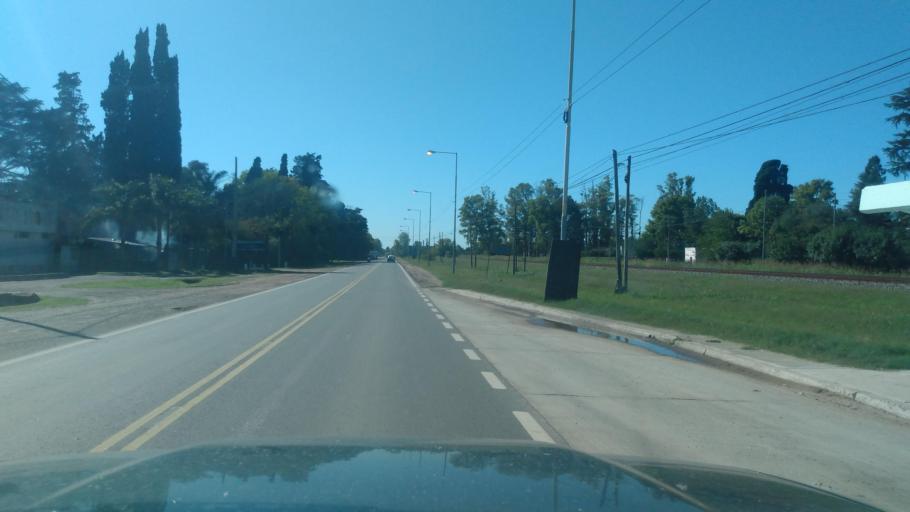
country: AR
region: Buenos Aires
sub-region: Partido de General Rodriguez
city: General Rodriguez
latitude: -34.6044
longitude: -58.9709
